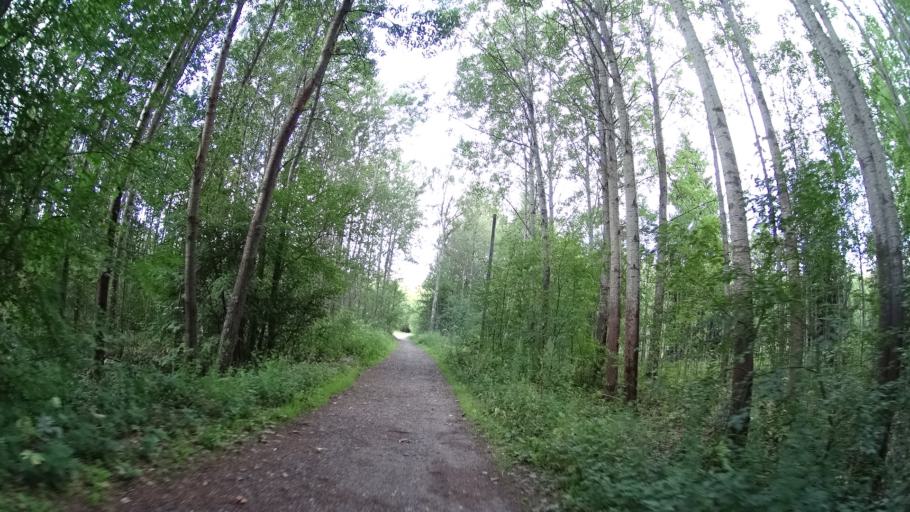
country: FI
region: Uusimaa
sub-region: Helsinki
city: Helsinki
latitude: 60.2757
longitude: 24.9061
